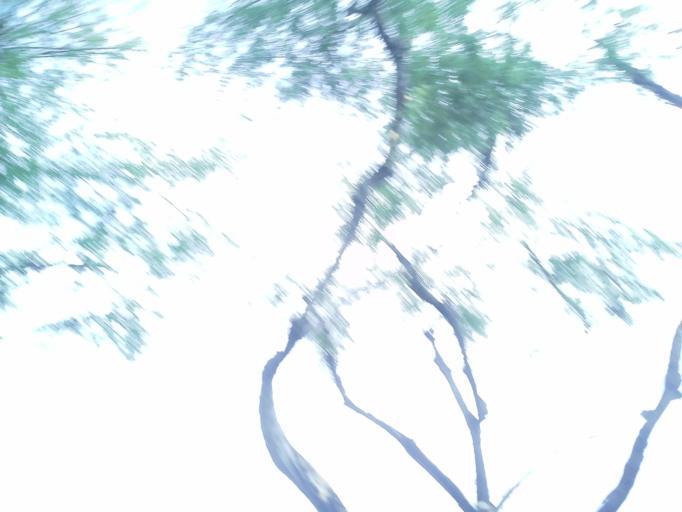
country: US
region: Arizona
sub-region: Maricopa County
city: Paradise Valley
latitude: 33.6776
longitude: -111.9733
